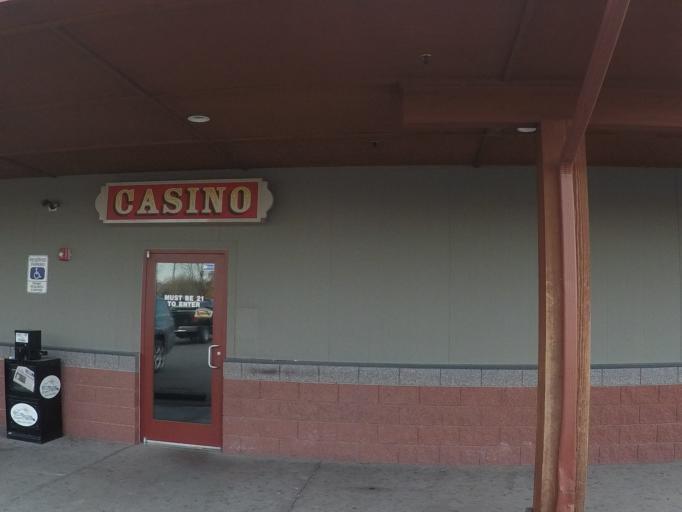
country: US
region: Montana
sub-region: Yellowstone County
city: Billings
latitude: 45.7631
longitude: -108.5385
